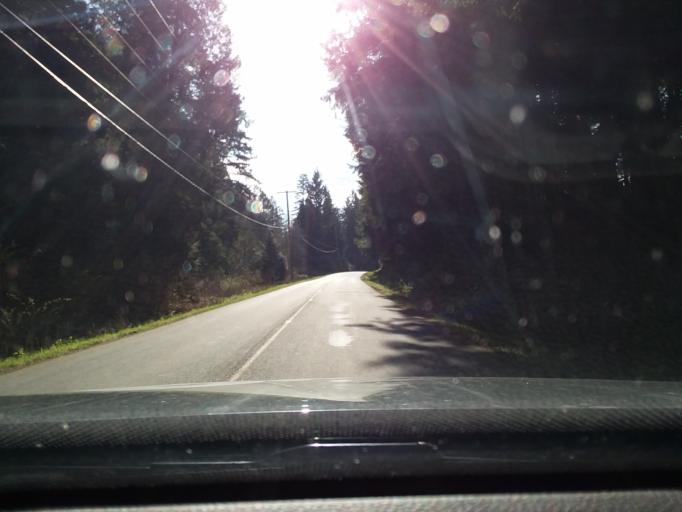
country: CA
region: British Columbia
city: North Cowichan
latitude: 48.9315
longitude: -123.4692
